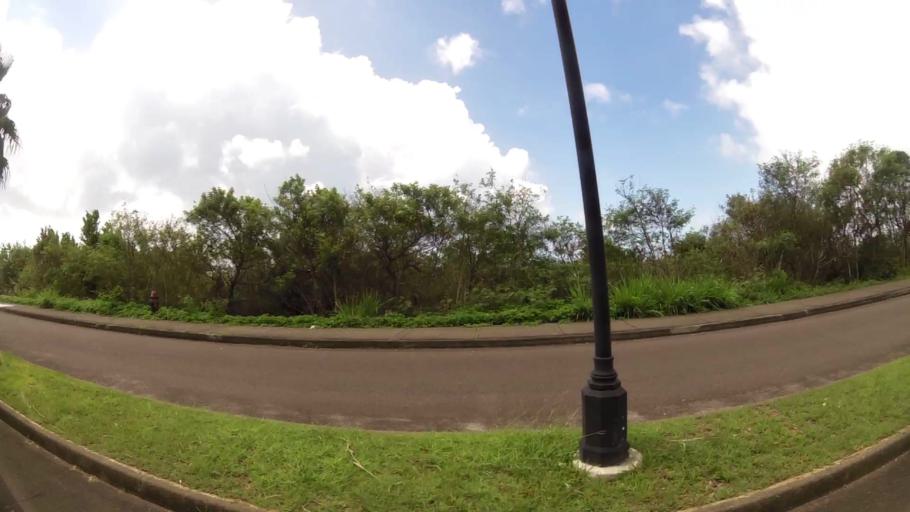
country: BM
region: Saint George
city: Saint George
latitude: 32.3661
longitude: -64.6734
